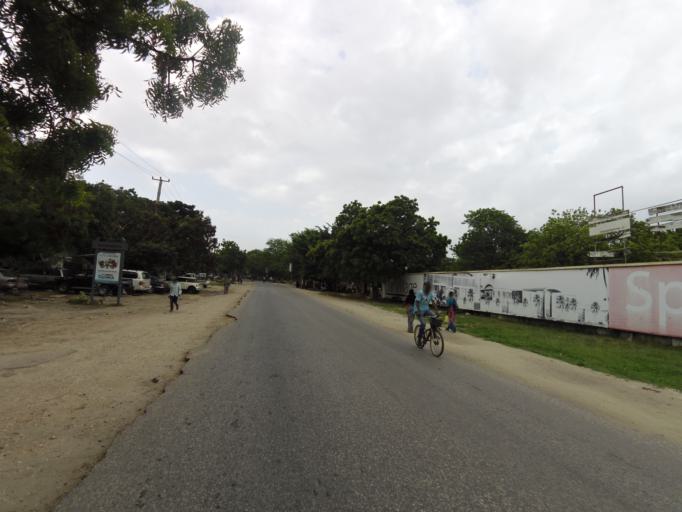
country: TZ
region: Dar es Salaam
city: Magomeni
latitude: -6.7726
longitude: 39.2438
